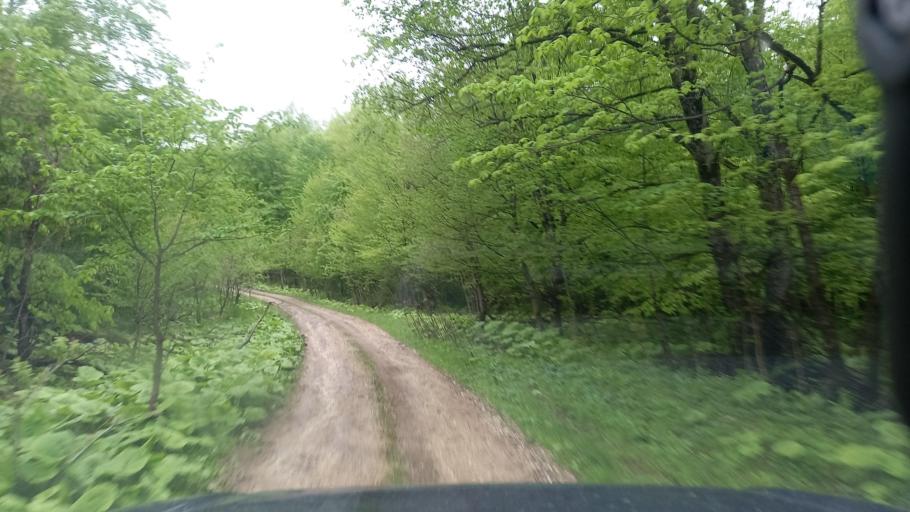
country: RU
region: Kabardino-Balkariya
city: Babugent
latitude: 43.2194
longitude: 43.5530
